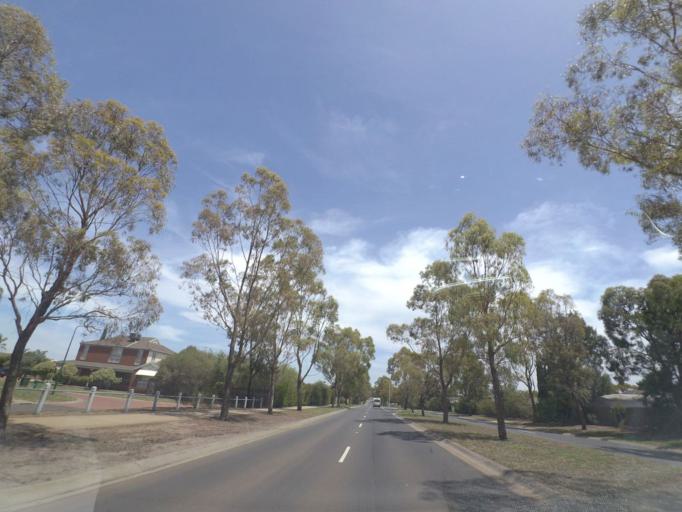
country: AU
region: Victoria
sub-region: Hume
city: Roxburgh Park
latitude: -37.6315
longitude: 144.9251
